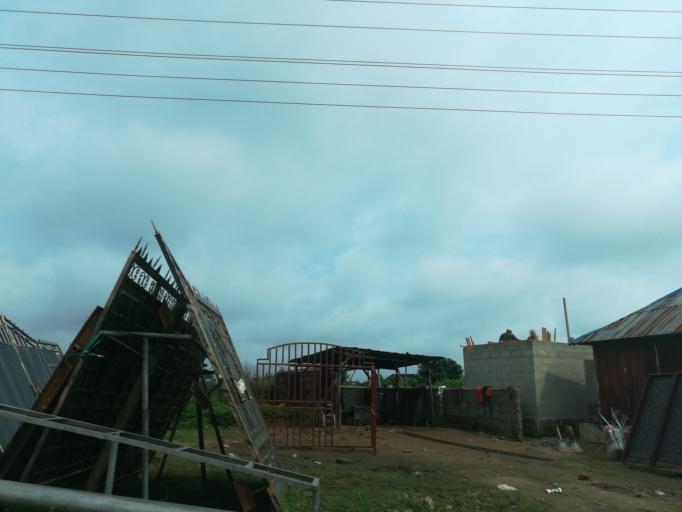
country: NG
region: Rivers
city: Emuoha
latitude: 4.8932
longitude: 6.9742
